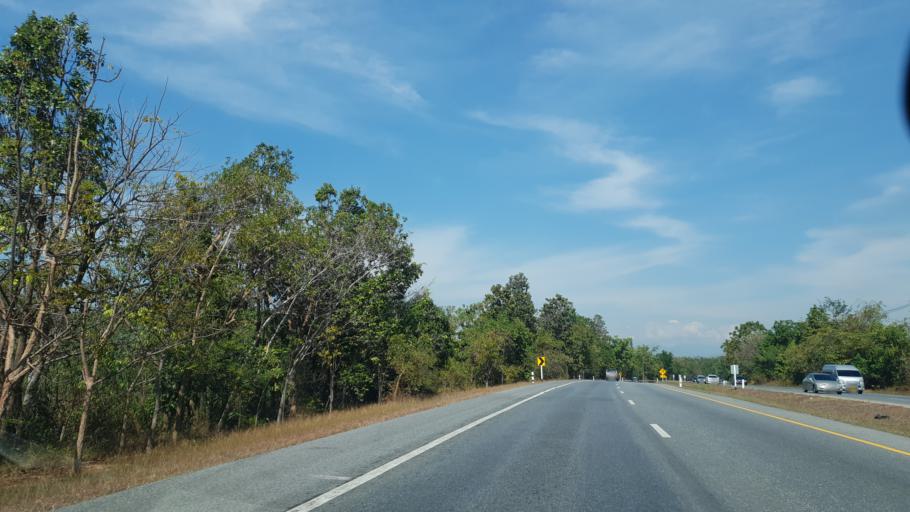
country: TH
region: Uttaradit
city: Thong Saen Khan
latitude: 17.4236
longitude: 100.2257
